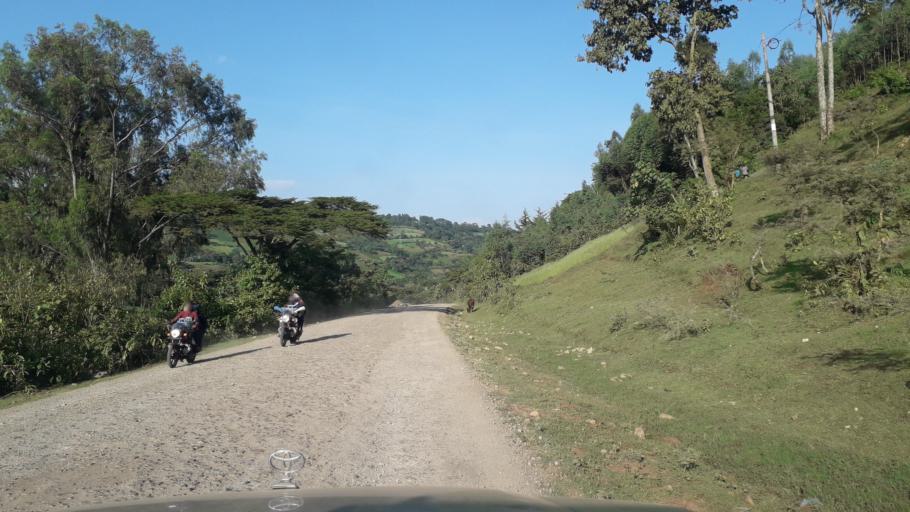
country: ET
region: Oromiya
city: Jima
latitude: 7.4769
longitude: 36.8774
